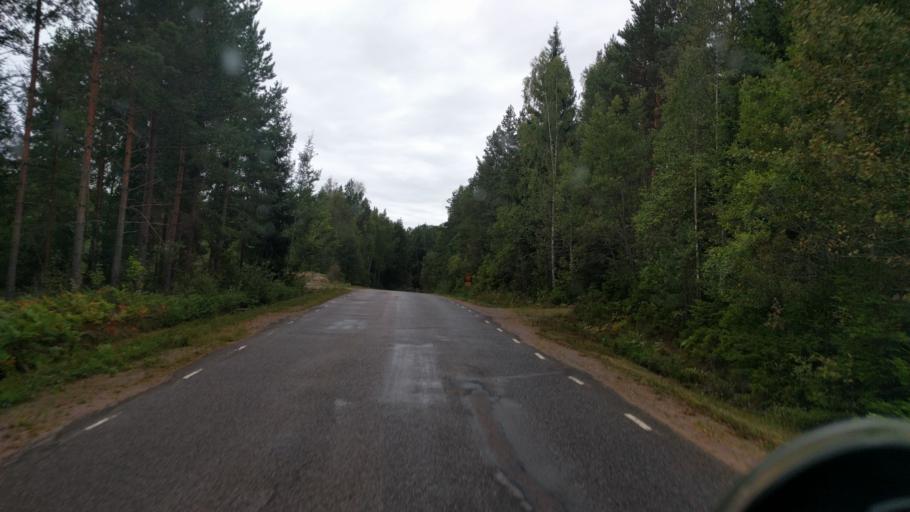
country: SE
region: Kalmar
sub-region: Vasterviks Kommun
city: Ankarsrum
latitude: 57.7043
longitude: 16.1607
